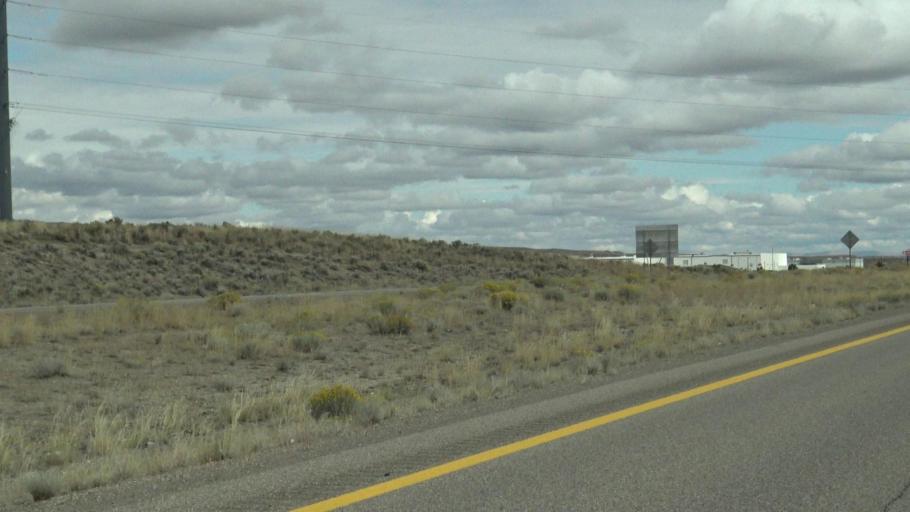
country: US
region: Nevada
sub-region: Elko County
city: Elko
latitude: 40.8602
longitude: -115.7381
